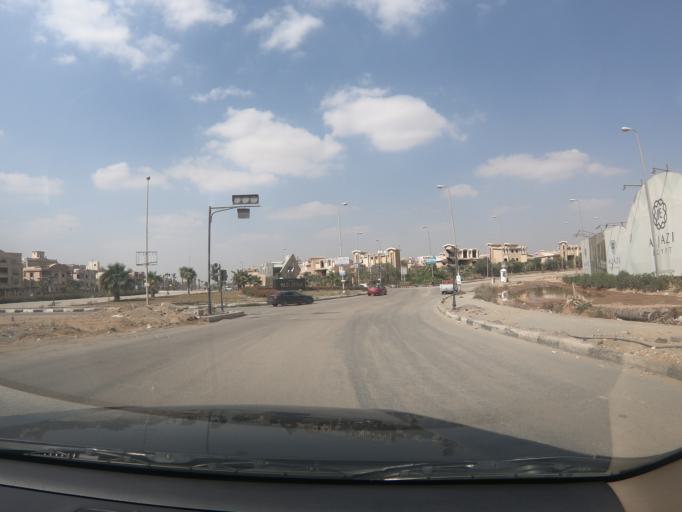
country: EG
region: Muhafazat al Qalyubiyah
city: Al Khankah
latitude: 30.0358
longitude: 31.4752
